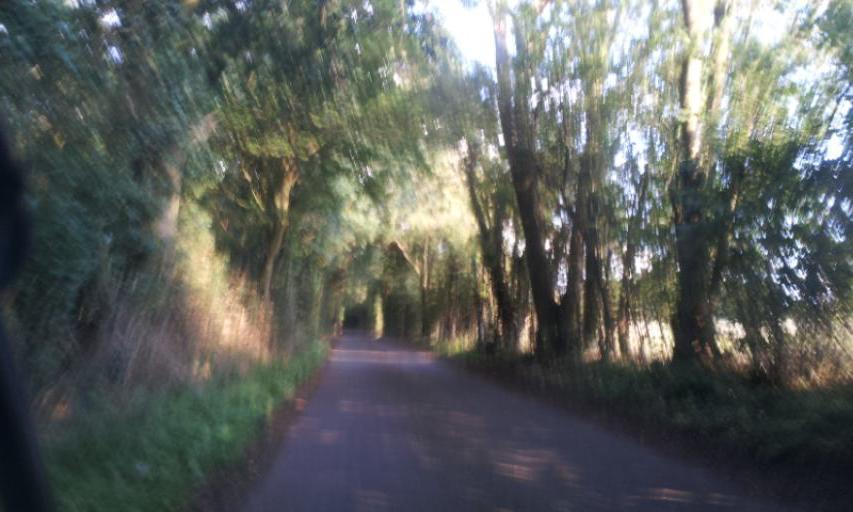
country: GB
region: England
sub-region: Kent
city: Meopham
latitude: 51.3883
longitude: 0.3649
